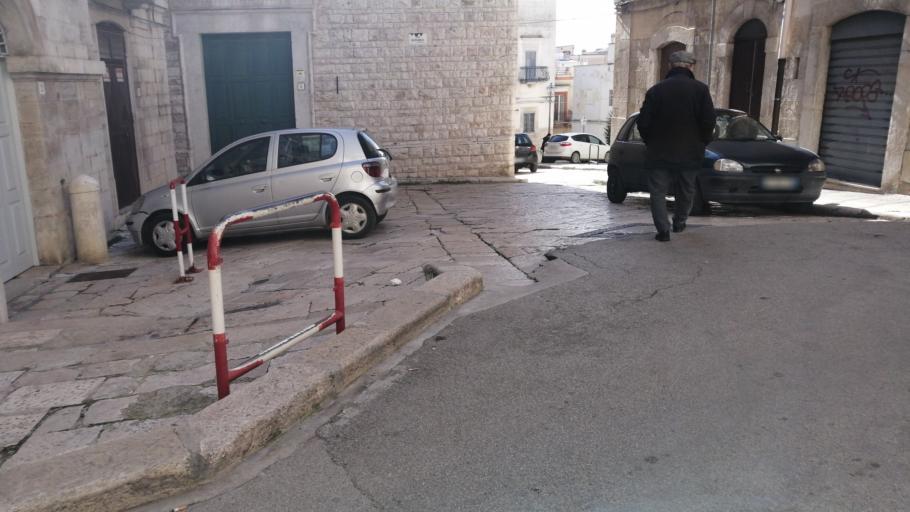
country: IT
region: Apulia
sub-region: Provincia di Barletta - Andria - Trani
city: Andria
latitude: 41.2252
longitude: 16.2951
